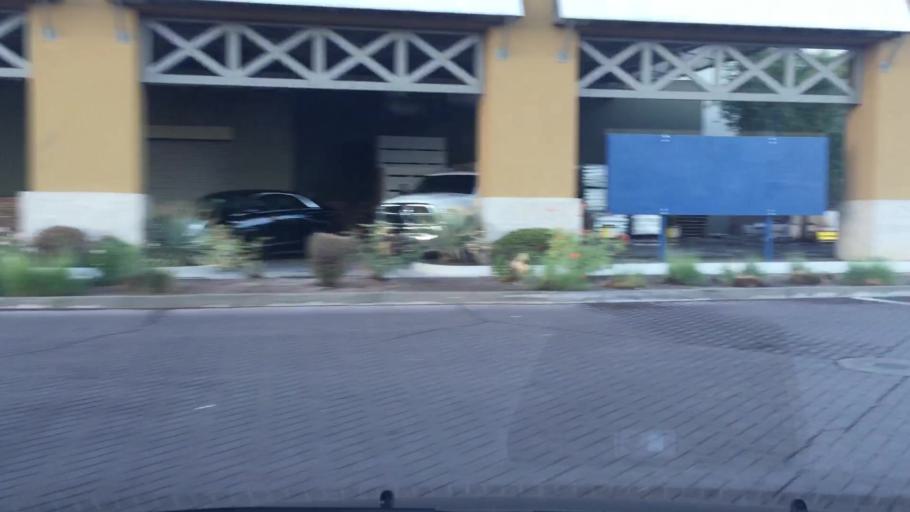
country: US
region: Arizona
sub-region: Maricopa County
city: Laveen
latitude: 33.3798
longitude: -112.1014
